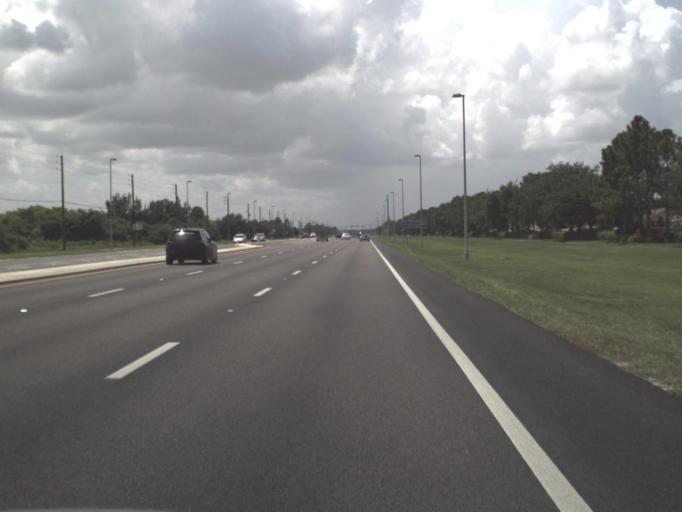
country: US
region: Florida
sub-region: Hillsborough County
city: Riverview
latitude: 27.8180
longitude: -82.3319
